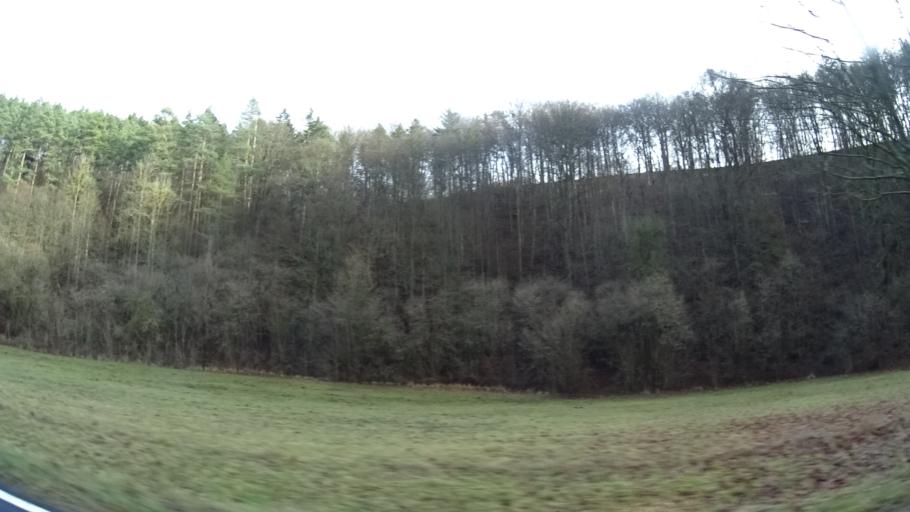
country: DE
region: Thuringia
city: Utendorf
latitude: 50.6016
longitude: 10.4434
